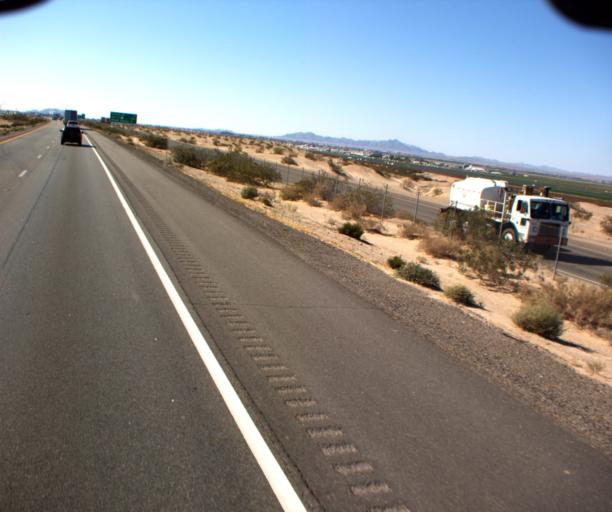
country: US
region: Arizona
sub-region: Yuma County
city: Yuma
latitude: 32.6861
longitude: -114.5674
